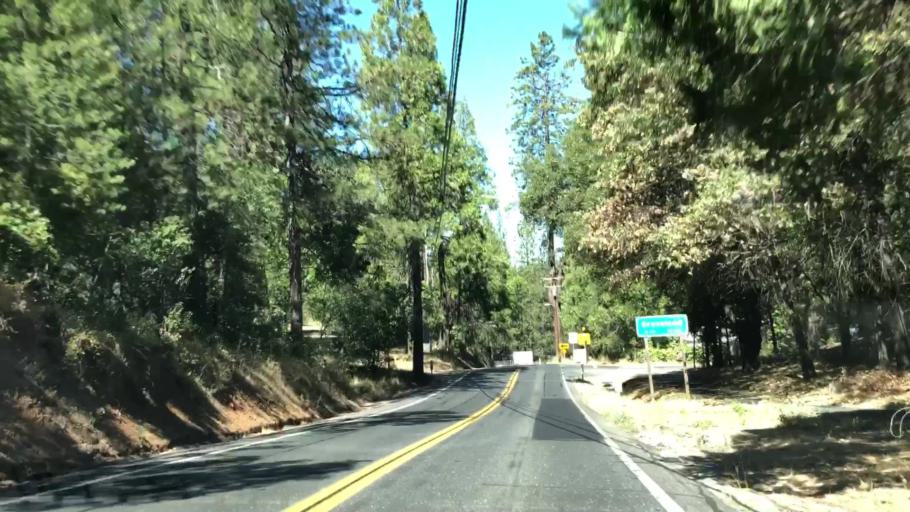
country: US
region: California
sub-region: Tuolumne County
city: Tuolumne City
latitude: 37.8391
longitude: -120.2228
